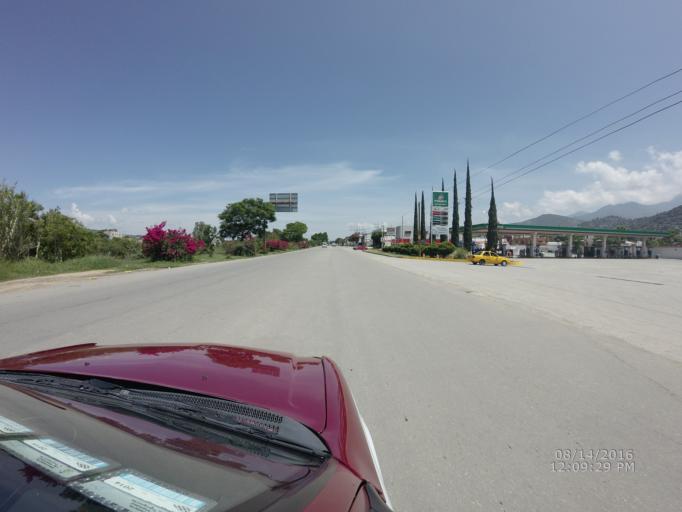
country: MX
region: Oaxaca
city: Oaxaca de Juarez
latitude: 17.0814
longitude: -96.7483
